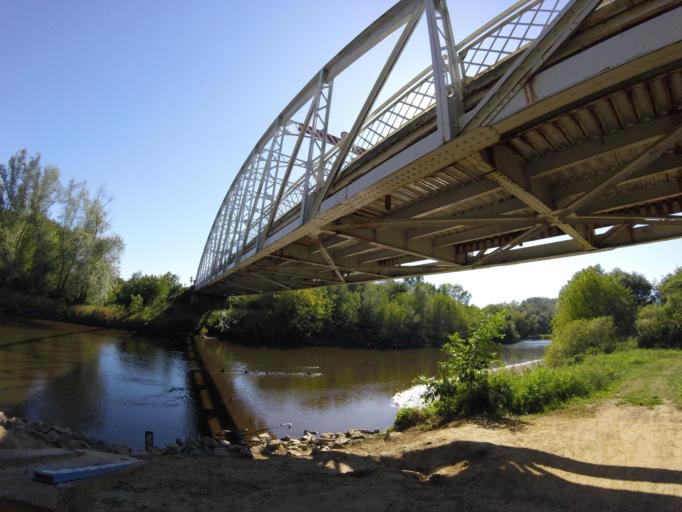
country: HU
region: Gyor-Moson-Sopron
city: Szany
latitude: 47.4413
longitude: 17.2103
